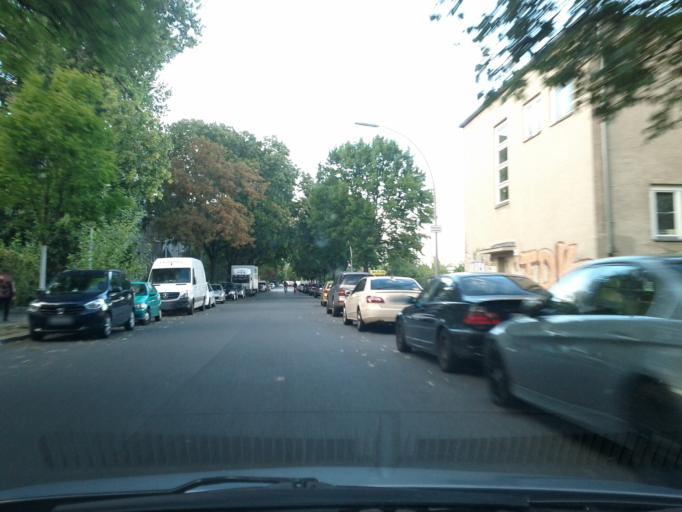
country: DE
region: Berlin
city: Treptow Bezirk
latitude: 52.4806
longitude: 13.4556
